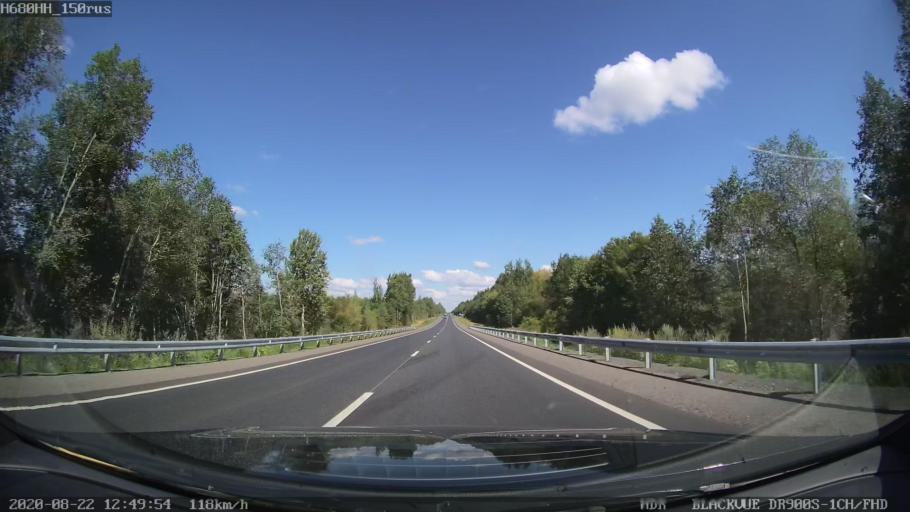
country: RU
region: Tverskaya
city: Rameshki
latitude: 57.4582
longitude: 36.2134
